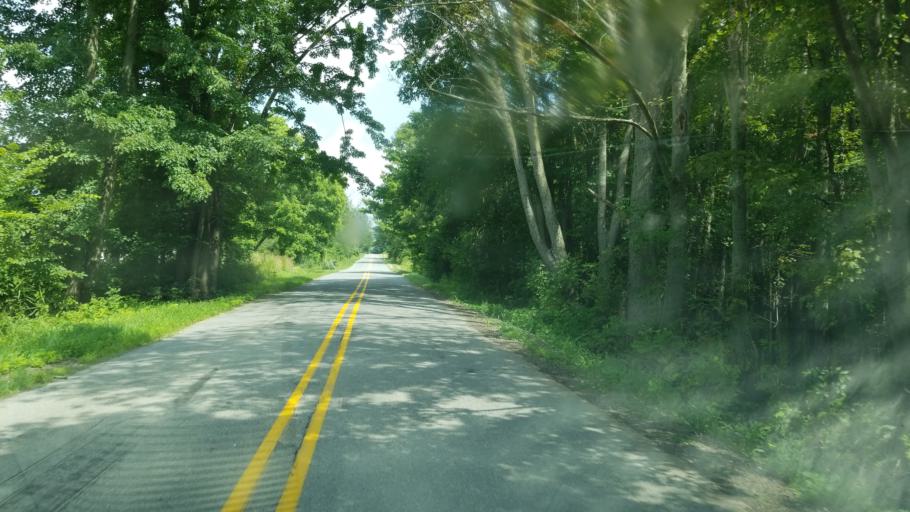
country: US
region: Michigan
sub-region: Kent County
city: Cedar Springs
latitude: 43.2637
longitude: -85.5113
